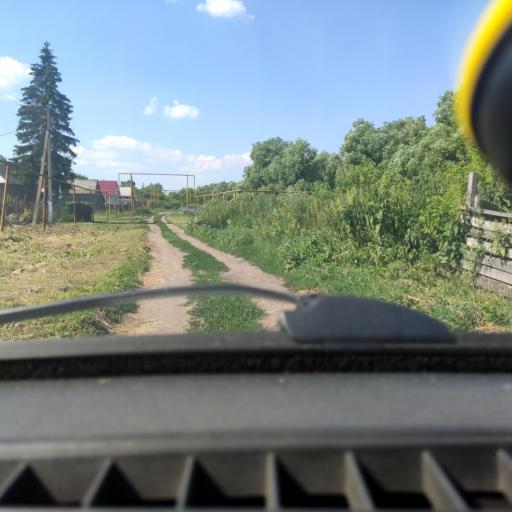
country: RU
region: Samara
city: Povolzhskiy
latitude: 53.7584
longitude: 49.7323
